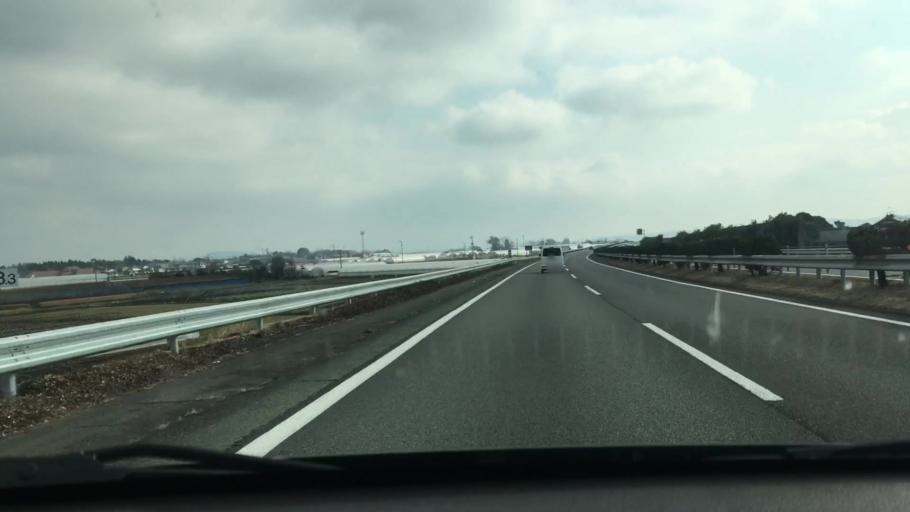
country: JP
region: Kumamoto
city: Ueki
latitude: 32.8863
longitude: 130.7247
